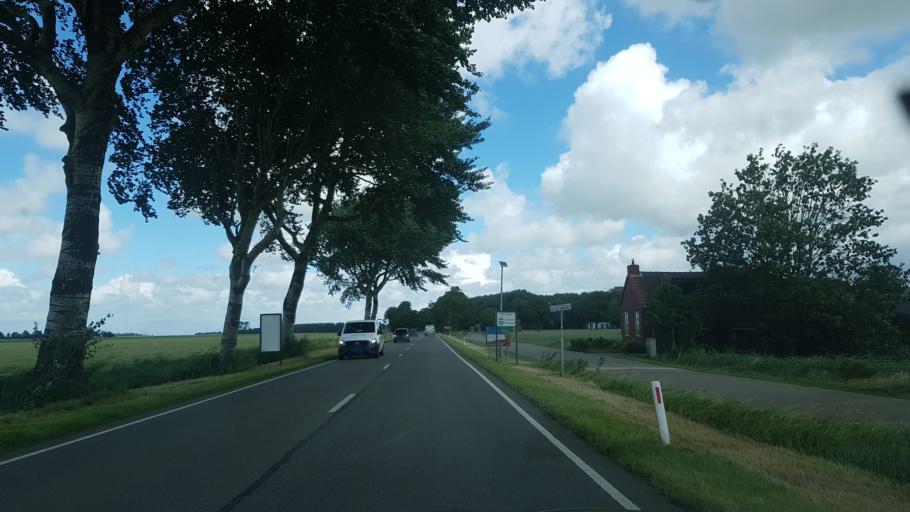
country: NL
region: Groningen
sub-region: Gemeente Winsum
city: Winsum
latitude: 53.3836
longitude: 6.5307
